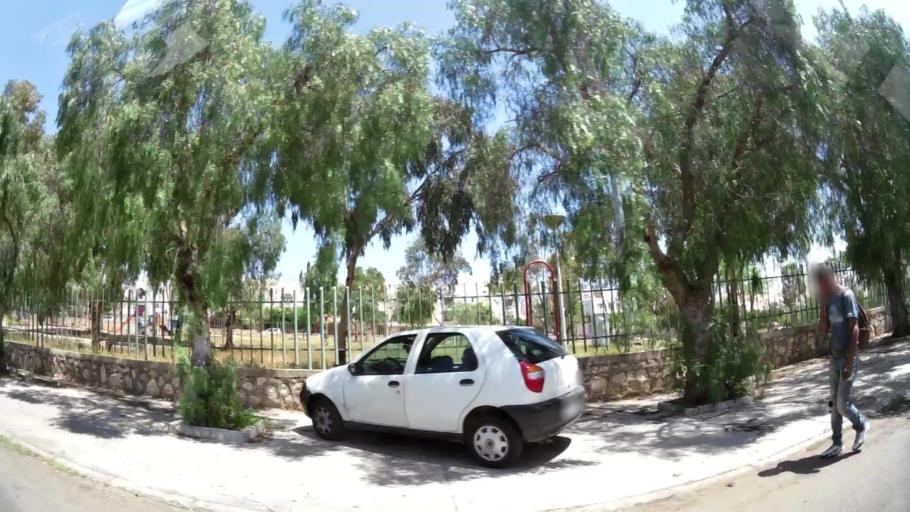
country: MA
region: Souss-Massa-Draa
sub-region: Agadir-Ida-ou-Tnan
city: Agadir
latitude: 30.4336
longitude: -9.5875
